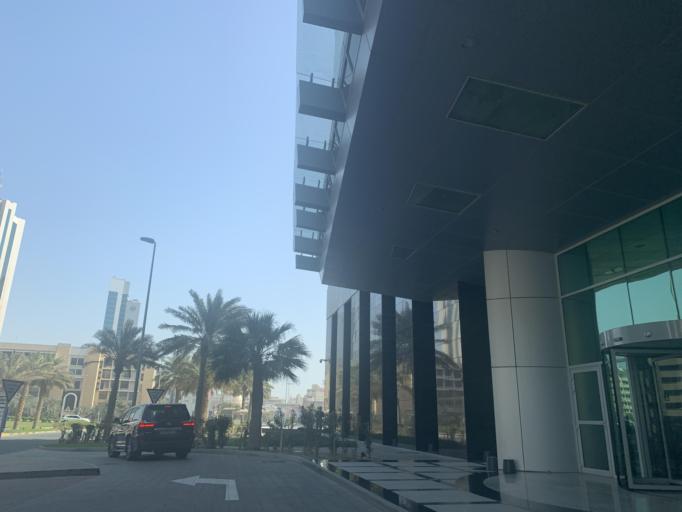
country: BH
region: Manama
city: Manama
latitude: 26.2383
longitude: 50.5744
